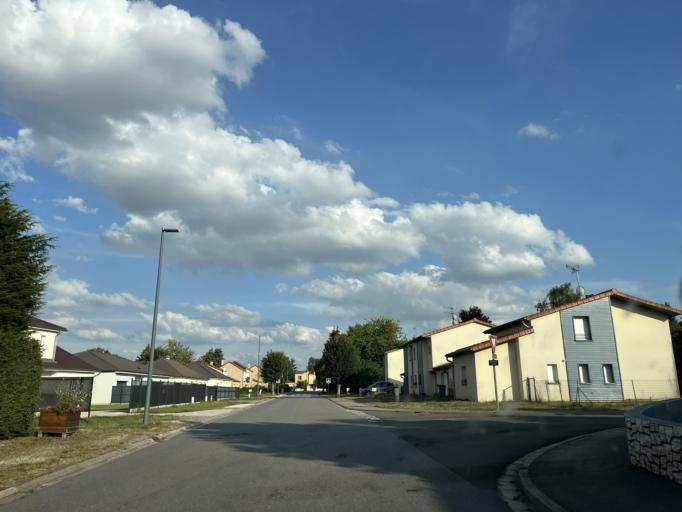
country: FR
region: Lorraine
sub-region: Departement de la Meuse
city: Clermont-en-Argonne
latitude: 49.1065
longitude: 5.0772
